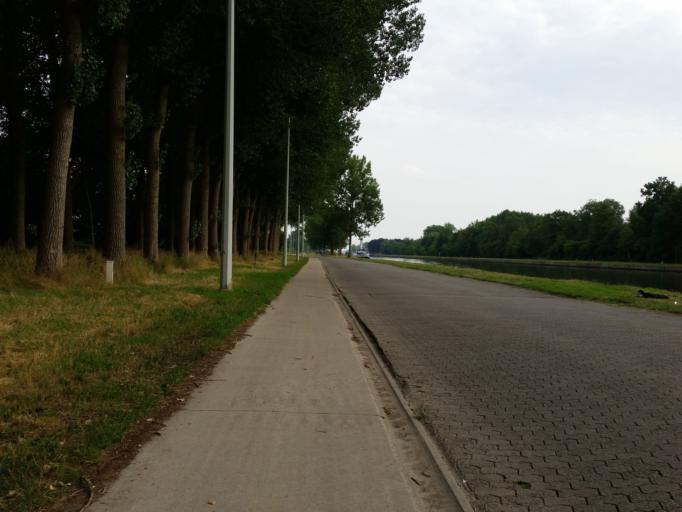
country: BE
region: Flanders
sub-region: Provincie Vlaams-Brabant
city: Kapelle-op-den-Bos
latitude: 50.9899
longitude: 4.3818
